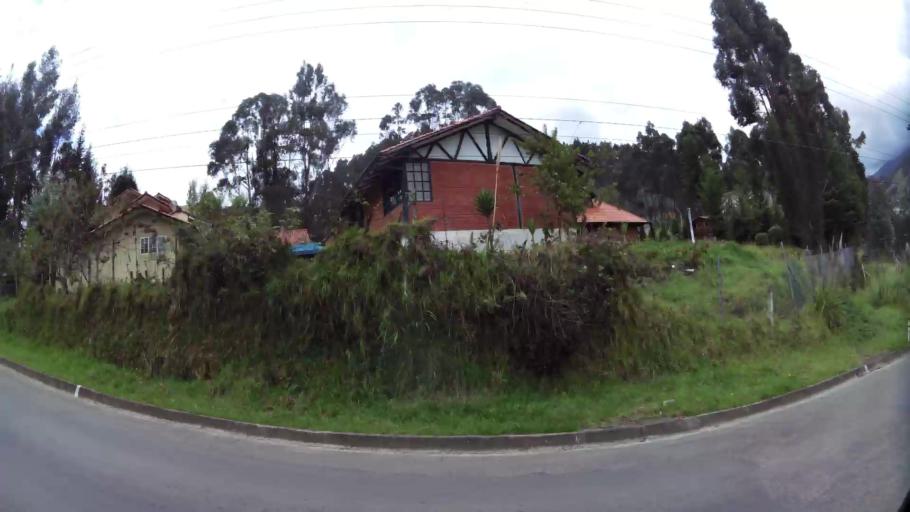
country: EC
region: Azuay
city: Cuenca
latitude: -2.8789
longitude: -79.0712
